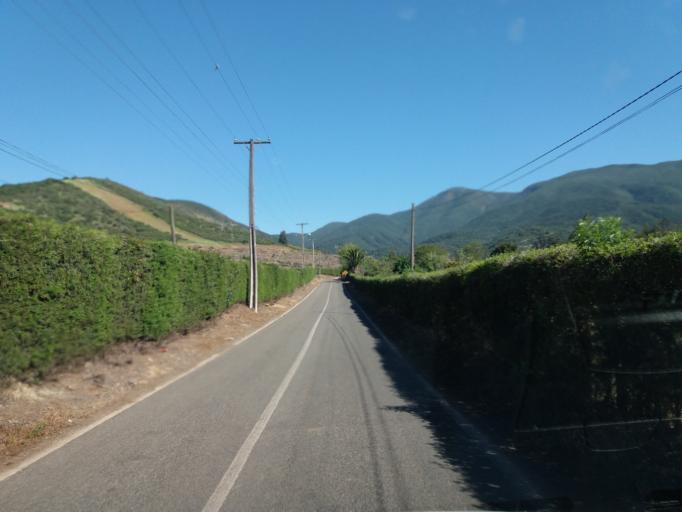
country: CL
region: Valparaiso
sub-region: Provincia de Quillota
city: Quillota
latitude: -32.8600
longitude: -71.2840
